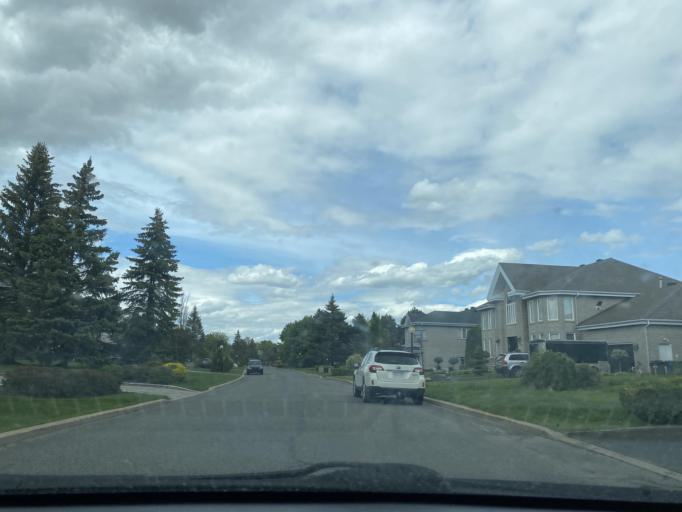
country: CA
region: Quebec
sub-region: Monteregie
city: Carignan
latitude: 45.4695
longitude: -73.2977
